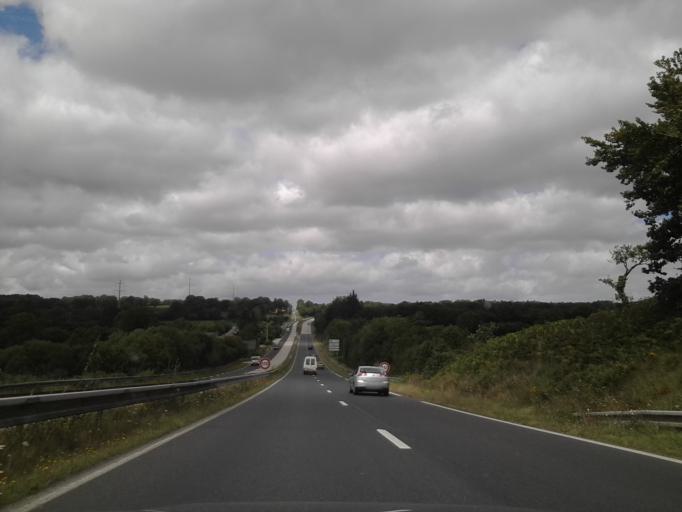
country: FR
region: Lower Normandy
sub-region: Departement de la Manche
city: Brix
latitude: 49.5537
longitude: -1.5619
